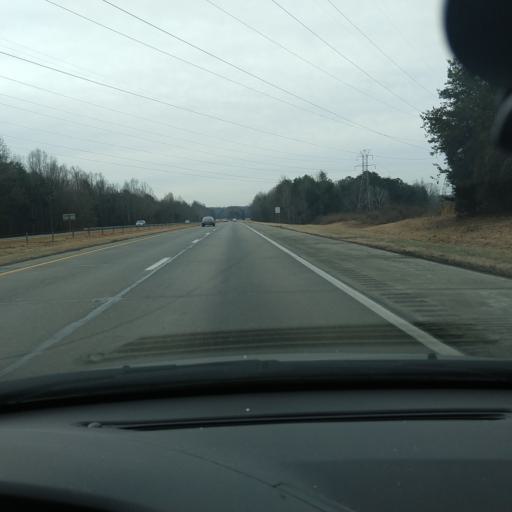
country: US
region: North Carolina
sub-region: Davidson County
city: Midway
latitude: 36.0056
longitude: -80.2367
